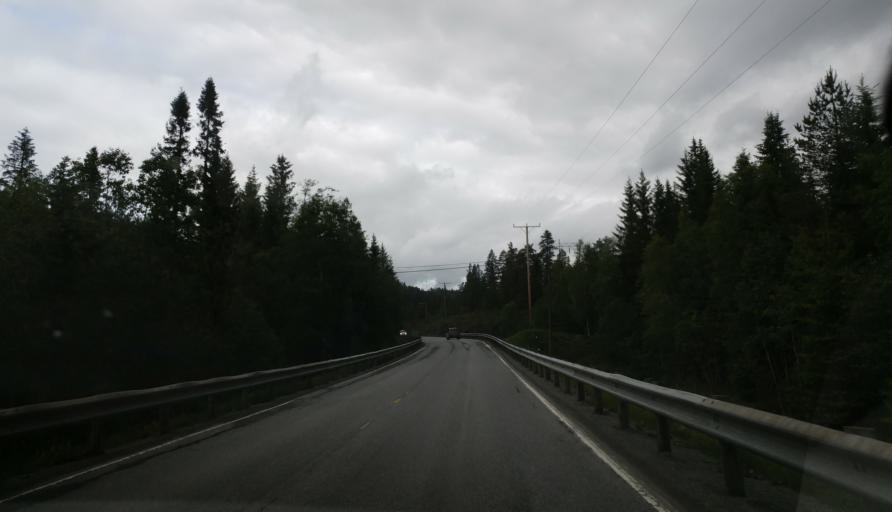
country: NO
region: Sor-Trondelag
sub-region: Selbu
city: Mebonden
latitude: 63.3511
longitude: 11.0773
